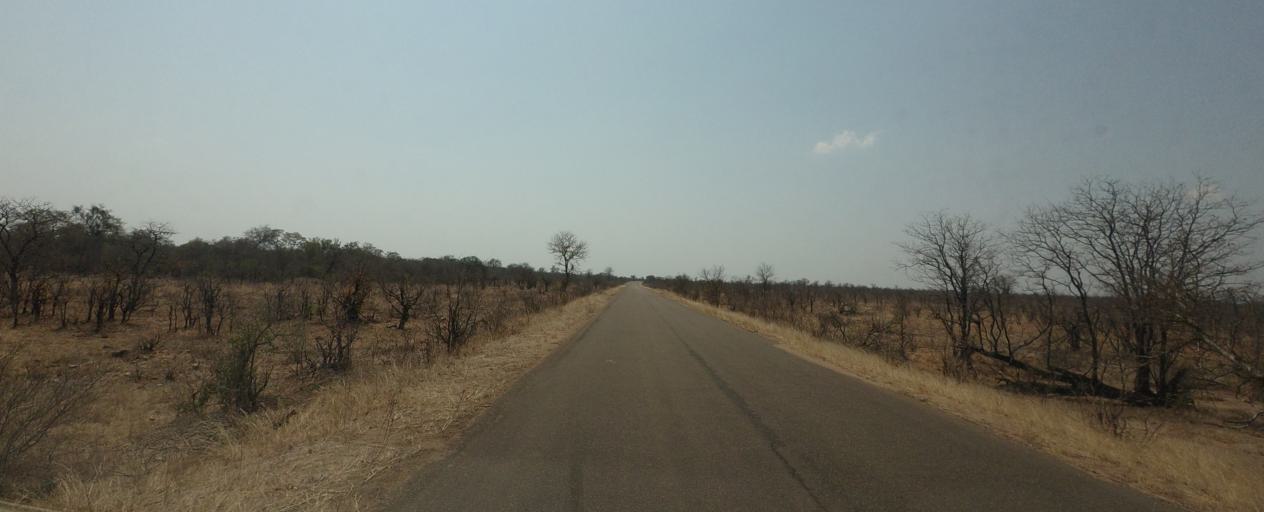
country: ZA
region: Limpopo
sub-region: Mopani District Municipality
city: Phalaborwa
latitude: -23.3809
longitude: 31.3252
